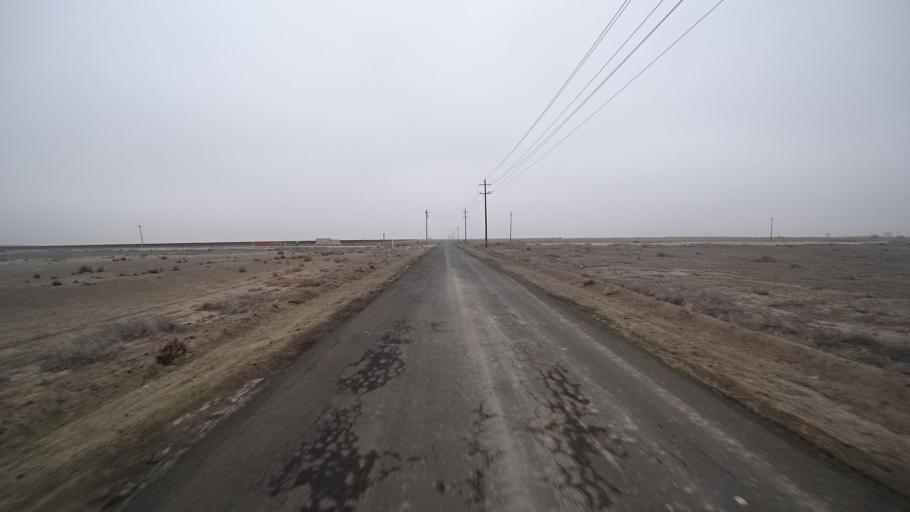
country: US
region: California
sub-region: Kern County
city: Lost Hills
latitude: 35.5949
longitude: -119.5805
